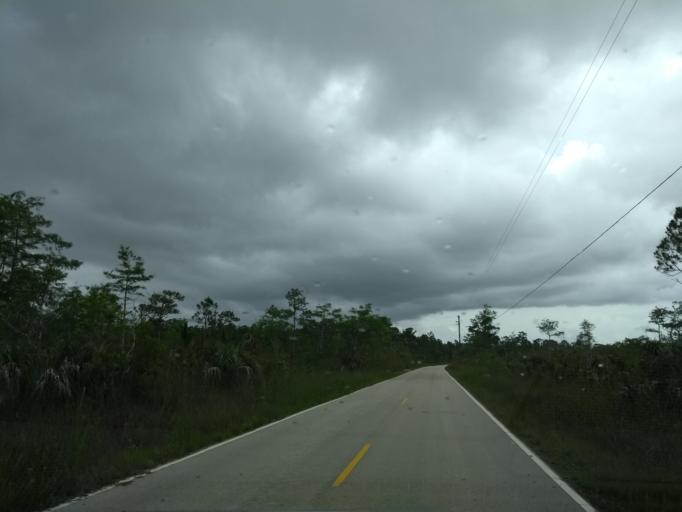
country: US
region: Florida
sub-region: Miami-Dade County
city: The Hammocks
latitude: 25.7546
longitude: -80.9333
